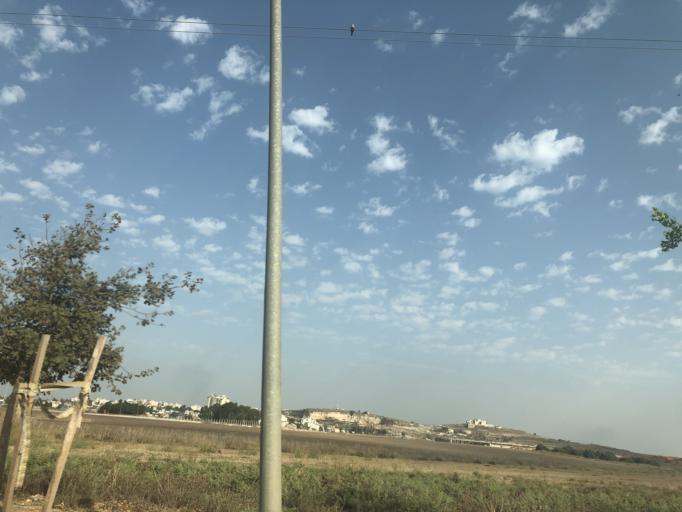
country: IL
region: Central District
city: Rosh Ha'Ayin
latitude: 32.0870
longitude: 34.9422
